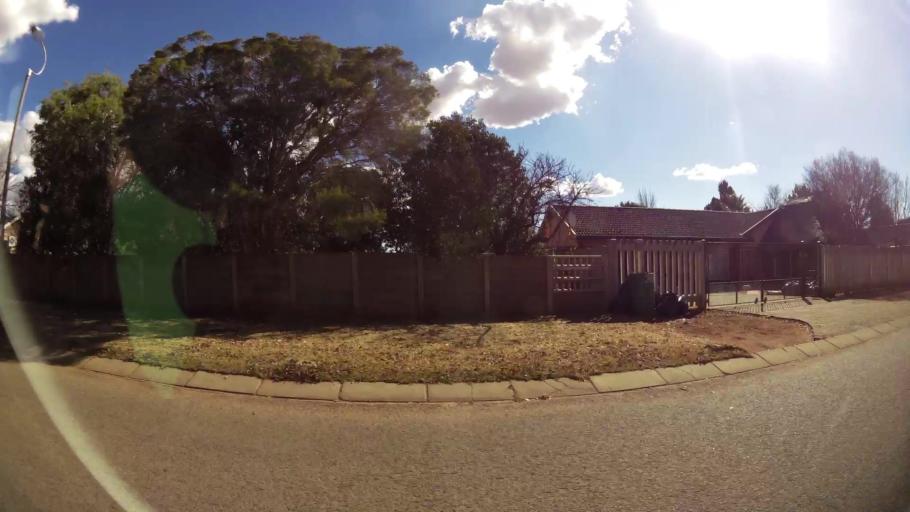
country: ZA
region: North-West
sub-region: Dr Kenneth Kaunda District Municipality
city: Klerksdorp
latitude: -26.8629
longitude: 26.6195
